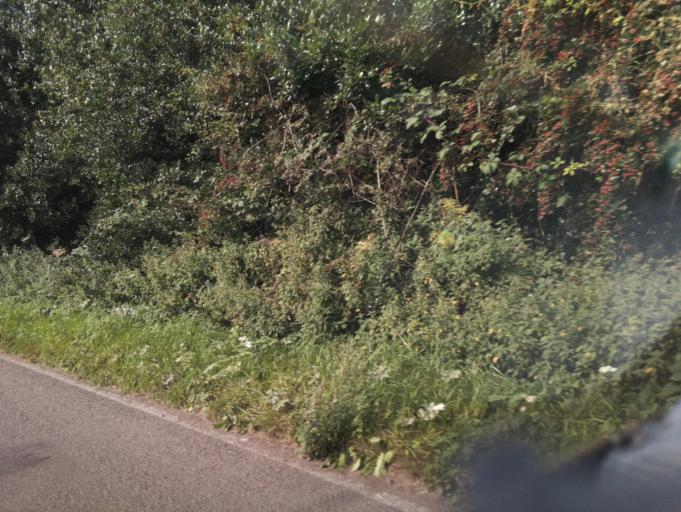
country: GB
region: England
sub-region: Walsall
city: Streetly
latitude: 52.6049
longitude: -1.8889
